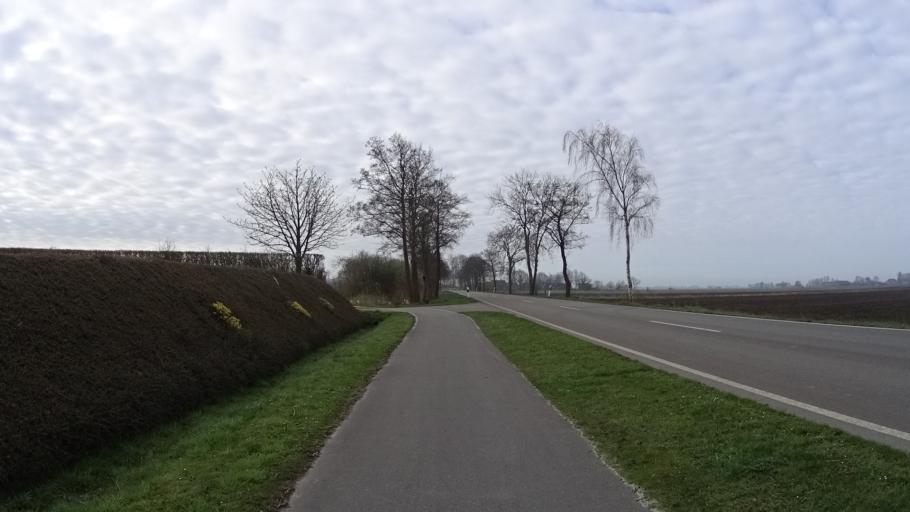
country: DE
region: Lower Saxony
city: Upgant-Schott
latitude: 53.4303
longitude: 7.3195
